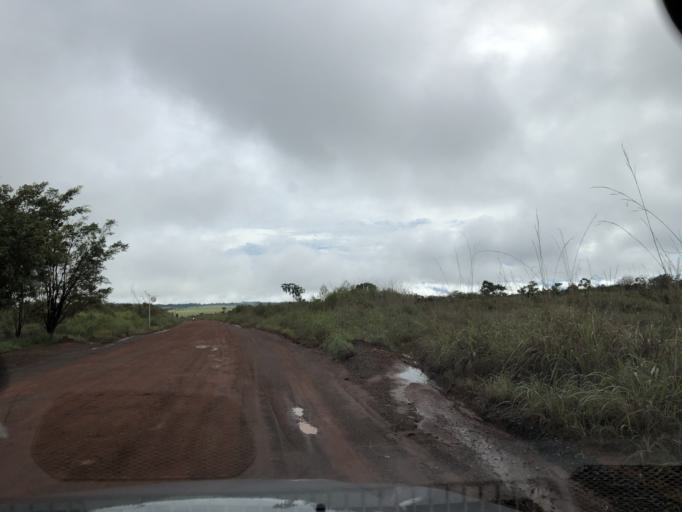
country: BR
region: Federal District
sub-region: Brasilia
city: Brasilia
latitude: -15.6122
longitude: -48.0448
